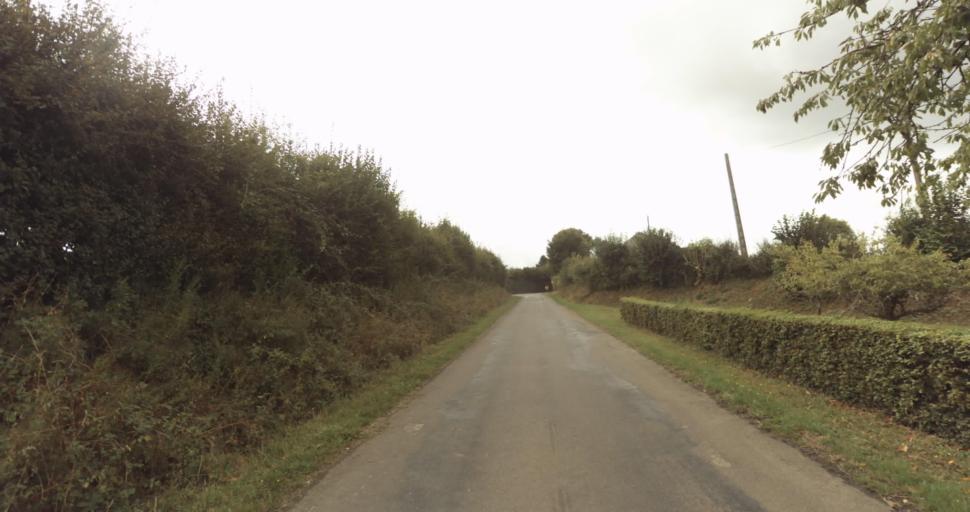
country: FR
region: Lower Normandy
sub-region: Departement de l'Orne
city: Gace
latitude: 48.8146
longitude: 0.3654
